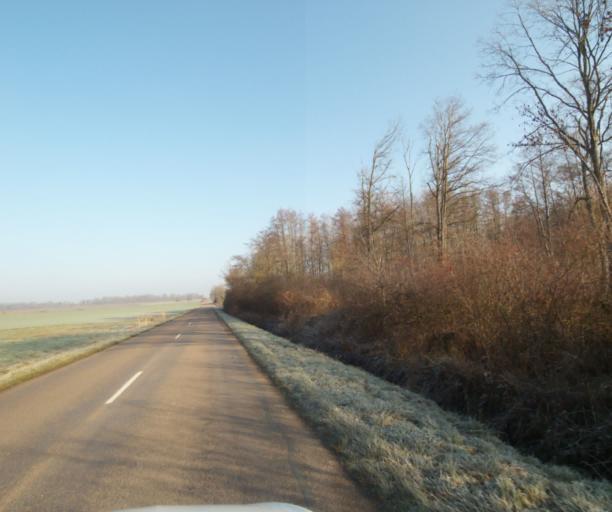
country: FR
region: Champagne-Ardenne
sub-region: Departement de la Haute-Marne
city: Montier-en-Der
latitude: 48.4203
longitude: 4.7450
